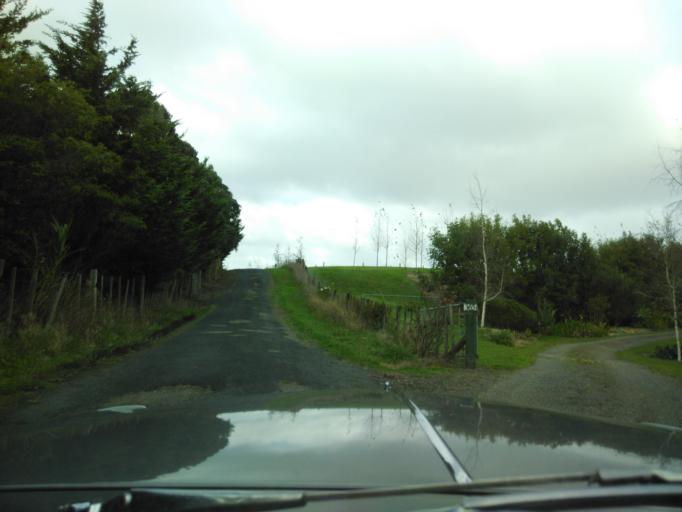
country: NZ
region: Auckland
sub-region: Auckland
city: Wellsford
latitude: -36.1779
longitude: 174.4144
